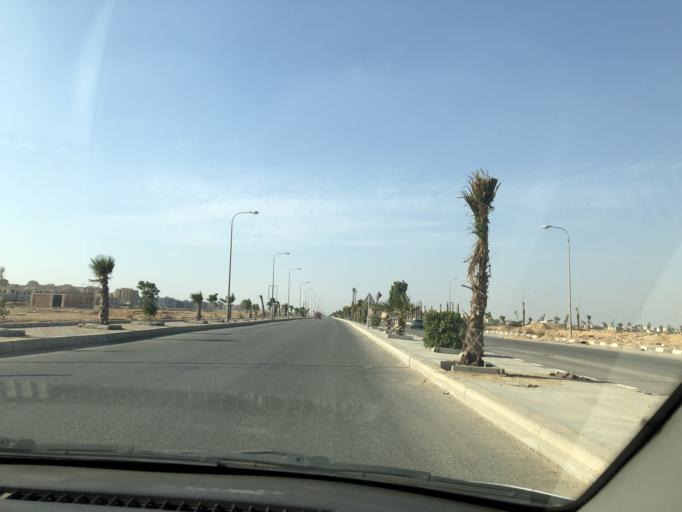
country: EG
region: Al Jizah
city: Madinat Sittah Uktubar
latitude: 29.9115
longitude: 31.0705
